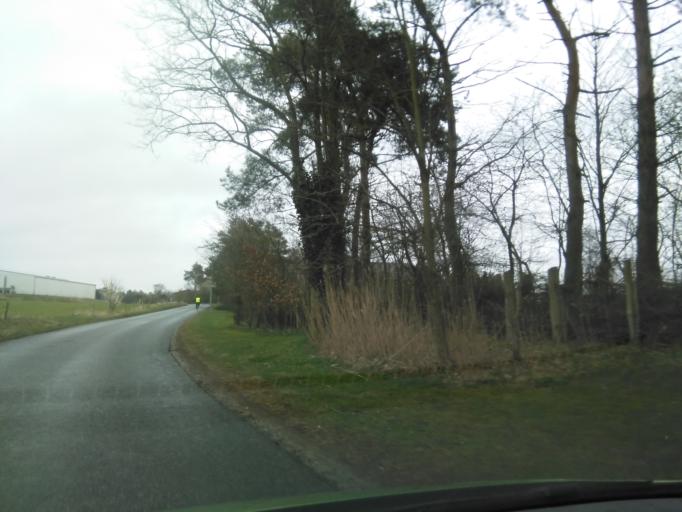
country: DK
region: Central Jutland
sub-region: Arhus Kommune
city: Kolt
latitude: 56.1444
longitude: 10.0529
